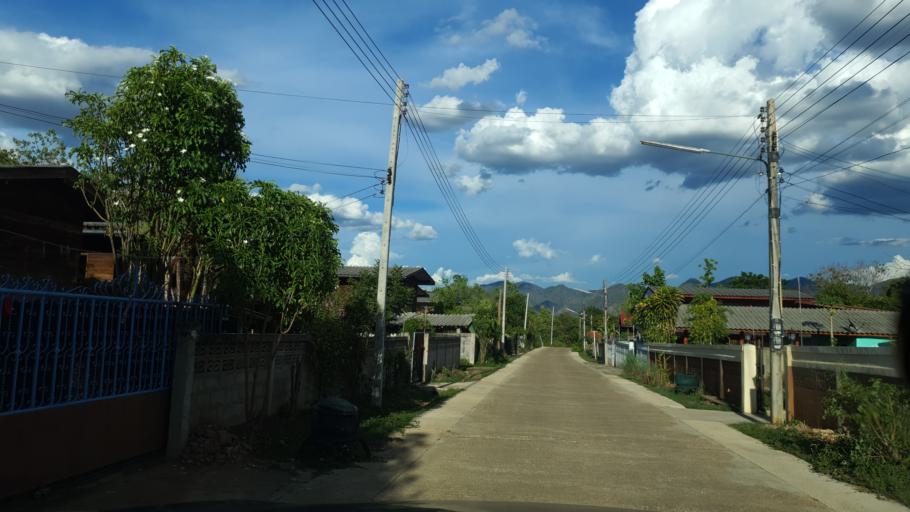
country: TH
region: Lampang
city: Sop Prap
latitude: 17.8754
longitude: 99.3022
